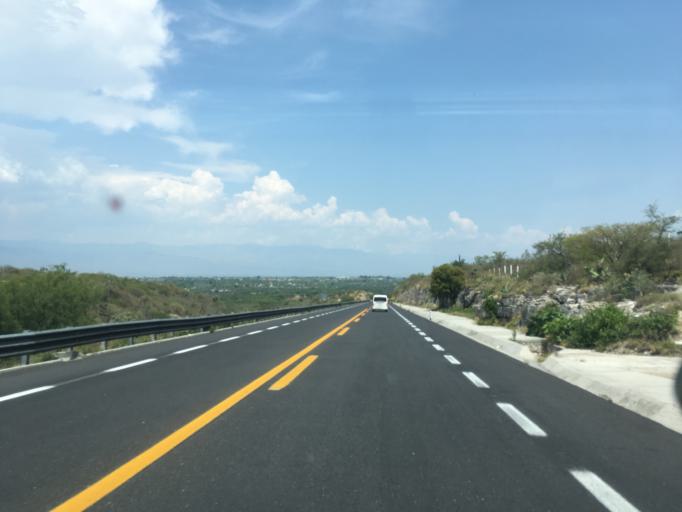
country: MX
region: Puebla
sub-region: Tehuacan
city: Santa Cruz Acapa
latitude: 18.3996
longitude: -97.3805
